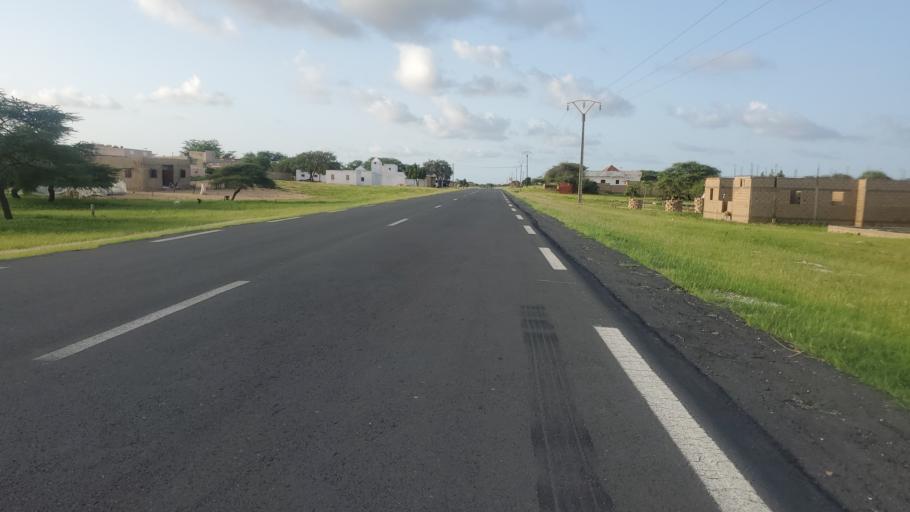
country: SN
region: Saint-Louis
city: Saint-Louis
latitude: 16.1515
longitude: -16.4097
